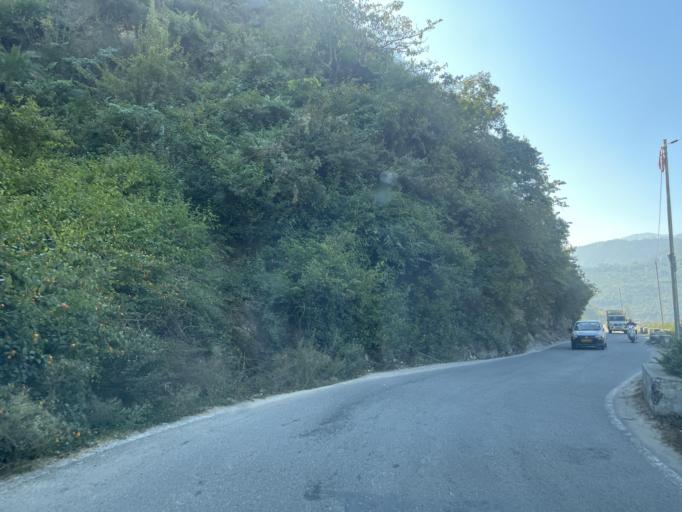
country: IN
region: Uttarakhand
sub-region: Naini Tal
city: Naini Tal
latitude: 29.5197
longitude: 79.4804
